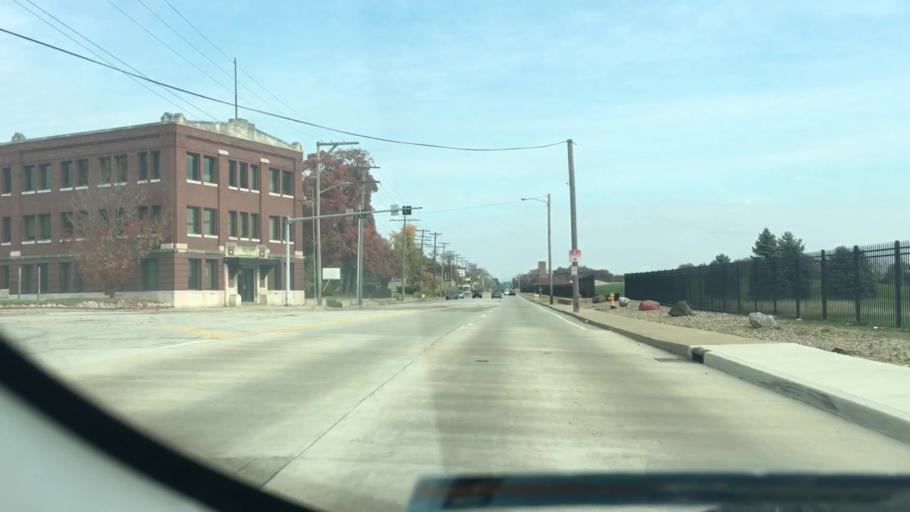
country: US
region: Illinois
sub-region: Peoria County
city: North Peoria
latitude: 40.7091
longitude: -89.5642
